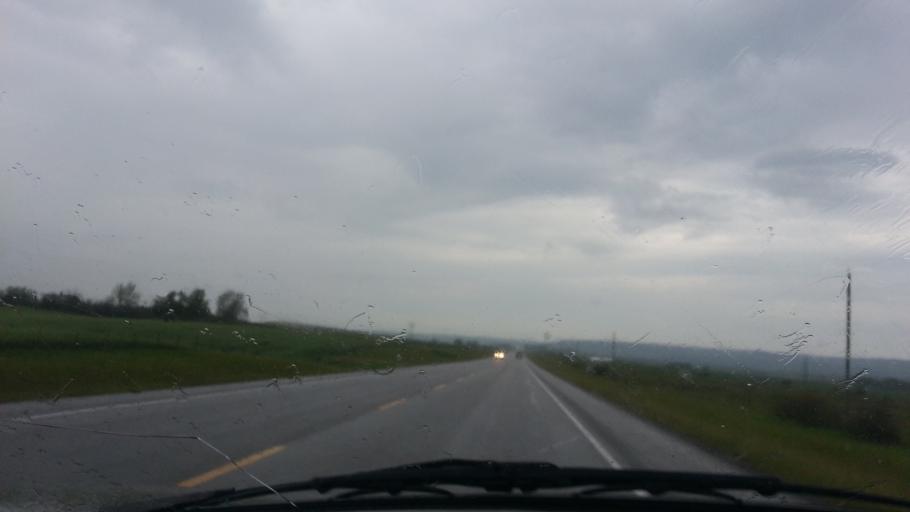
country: CA
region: Alberta
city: Cochrane
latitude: 51.1144
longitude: -114.4668
